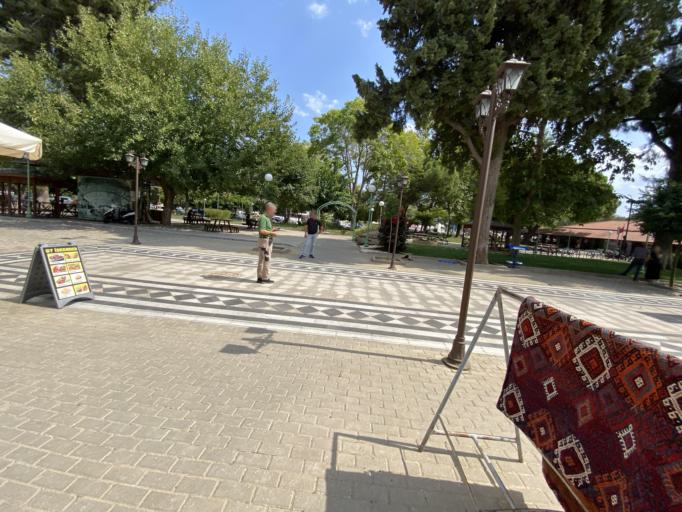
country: TR
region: Izmir
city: Selcuk
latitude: 37.9491
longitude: 27.3681
